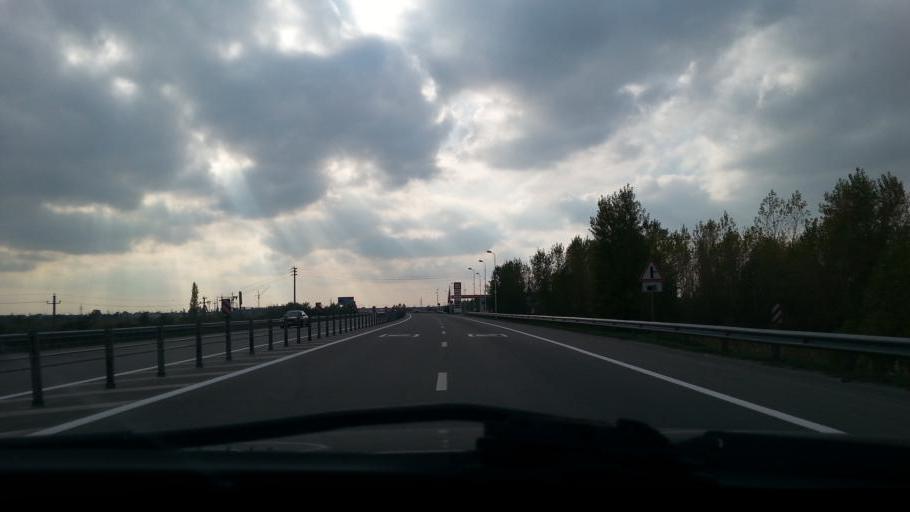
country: RU
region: Rostov
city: Bataysk
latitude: 47.1543
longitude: 39.7211
